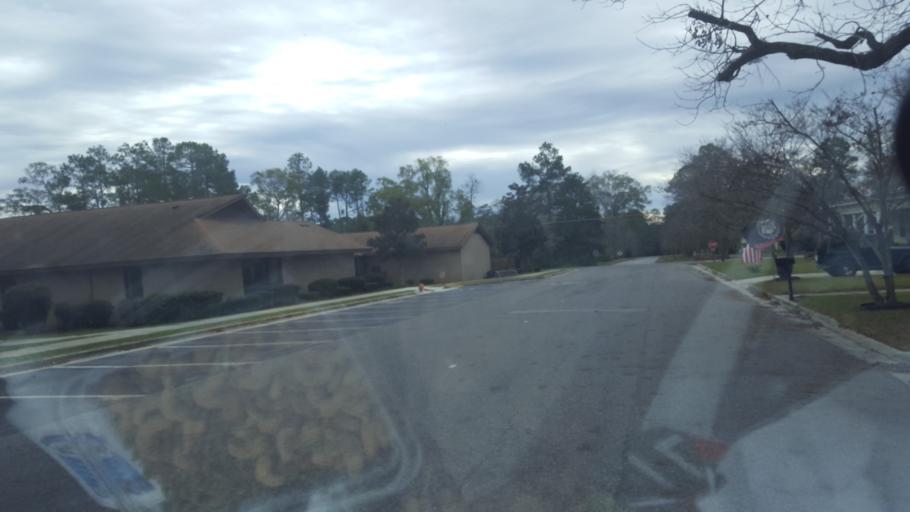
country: US
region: Georgia
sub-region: Irwin County
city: Ocilla
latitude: 31.5920
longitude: -83.2519
